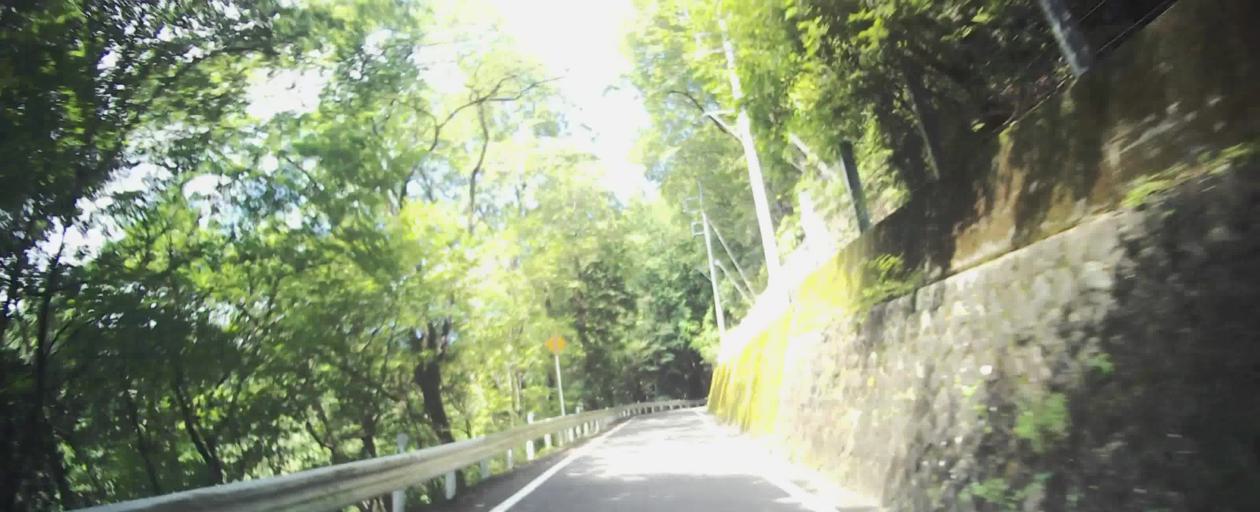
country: JP
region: Gunma
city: Kanekomachi
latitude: 36.4467
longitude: 138.9055
